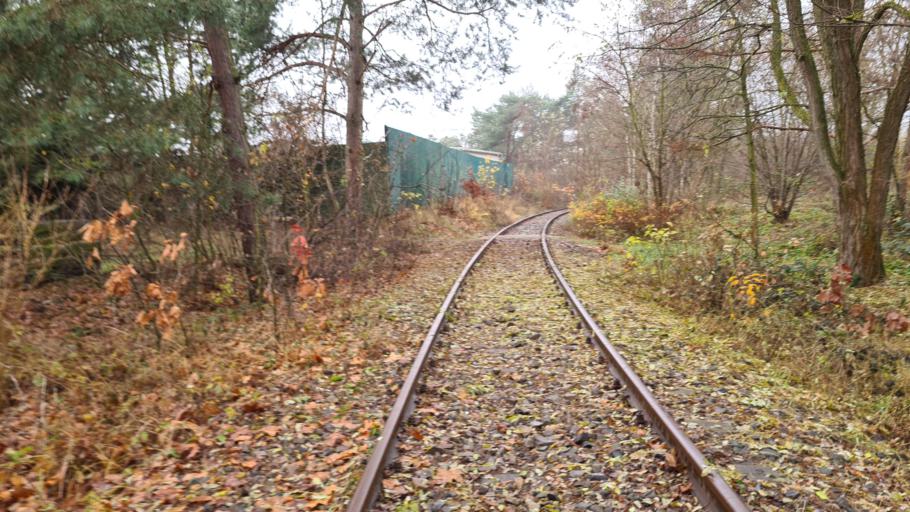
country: DE
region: Brandenburg
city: Sallgast
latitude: 51.5925
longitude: 13.7842
